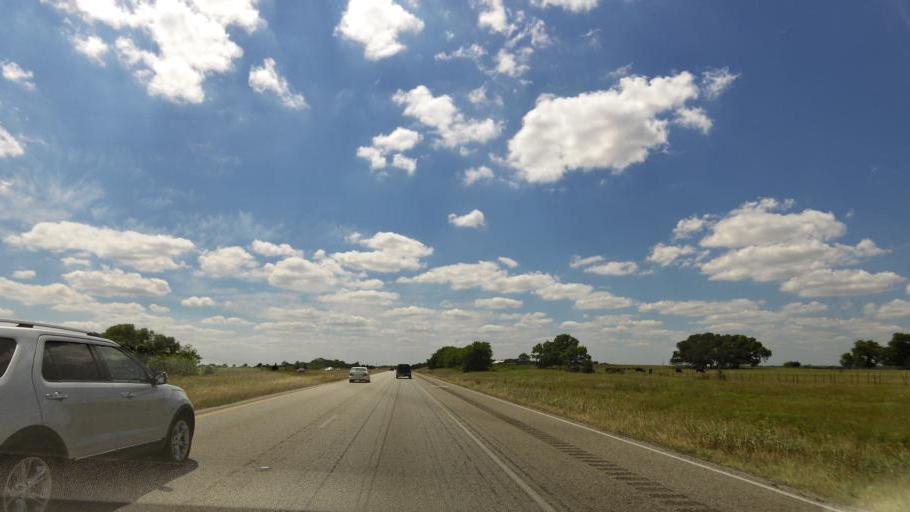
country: US
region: Texas
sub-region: Fayette County
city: Schulenburg
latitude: 29.6902
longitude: -96.9692
